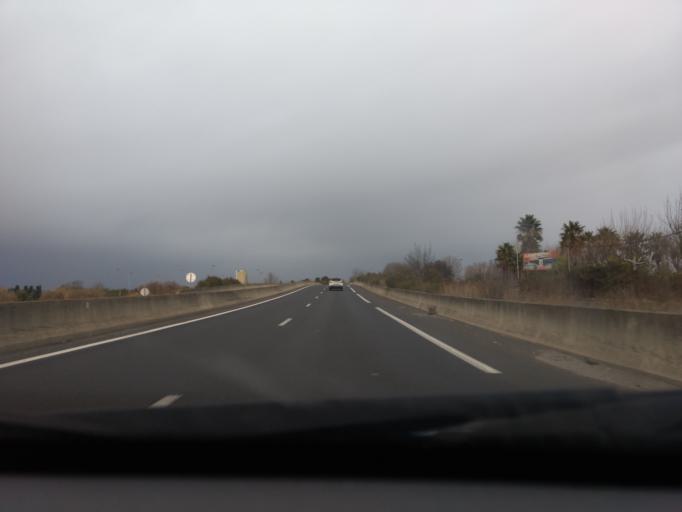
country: FR
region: Languedoc-Roussillon
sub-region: Departement de l'Herault
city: Lattes
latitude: 43.5532
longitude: 3.8933
